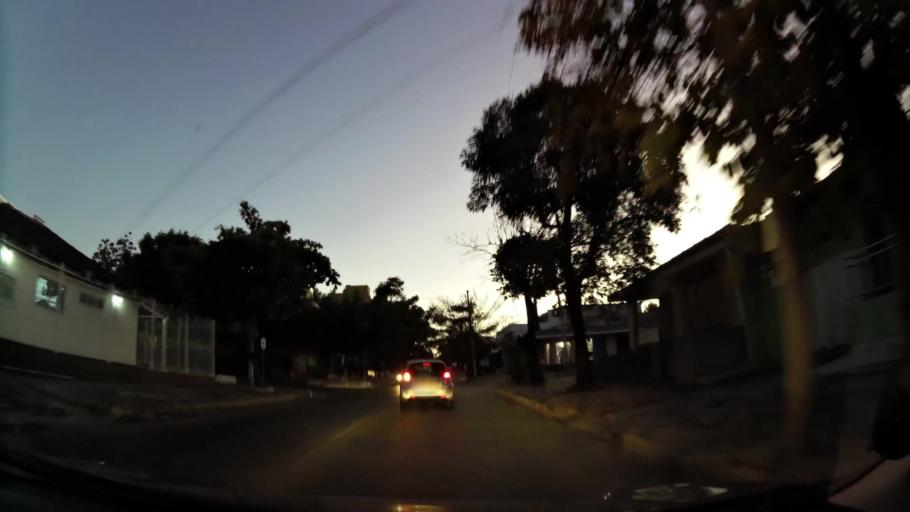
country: CO
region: Atlantico
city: Barranquilla
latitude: 10.9830
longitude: -74.7994
